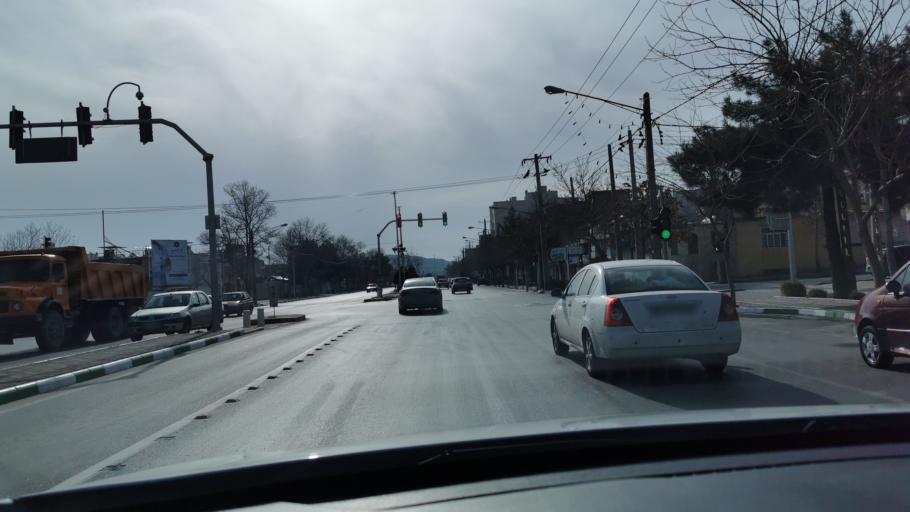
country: IR
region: Razavi Khorasan
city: Mashhad
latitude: 36.2876
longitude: 59.5434
